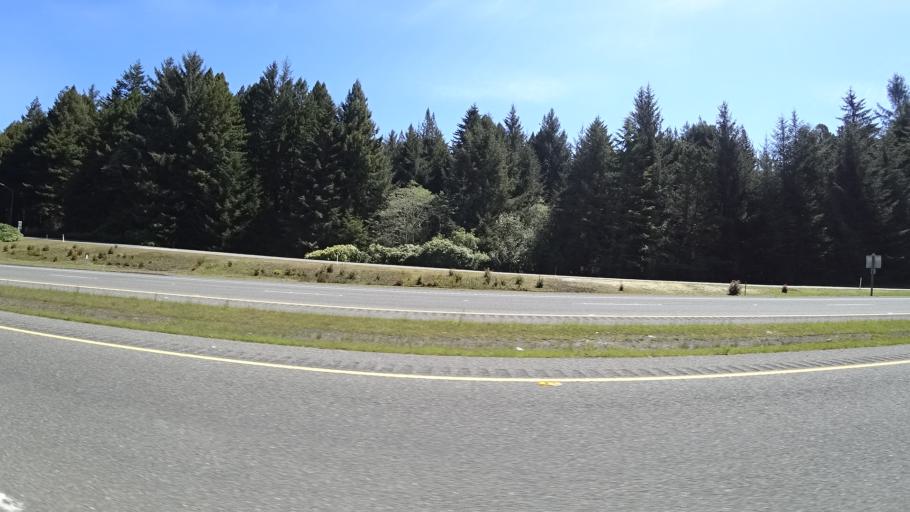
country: US
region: California
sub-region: Humboldt County
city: Westhaven-Moonstone
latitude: 41.1223
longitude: -124.1510
